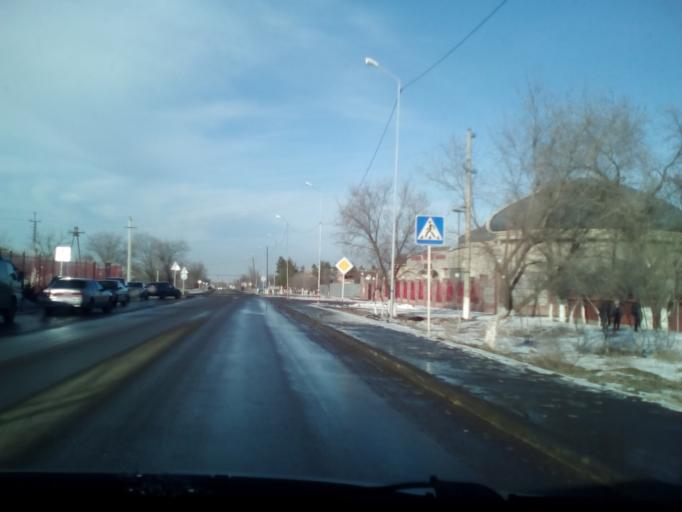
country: KZ
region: Almaty Oblysy
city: Burunday
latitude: 43.1827
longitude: 76.4144
